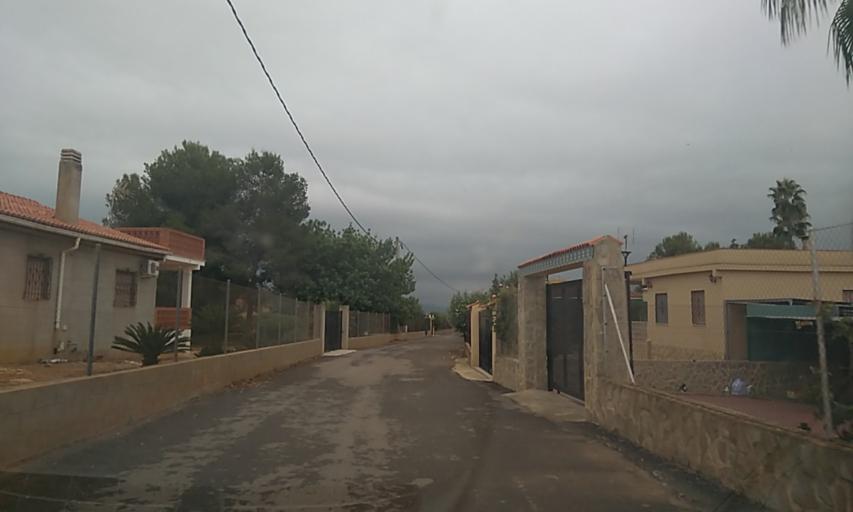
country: ES
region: Valencia
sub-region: Provincia de Valencia
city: Benimodo
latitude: 39.1907
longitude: -0.5576
